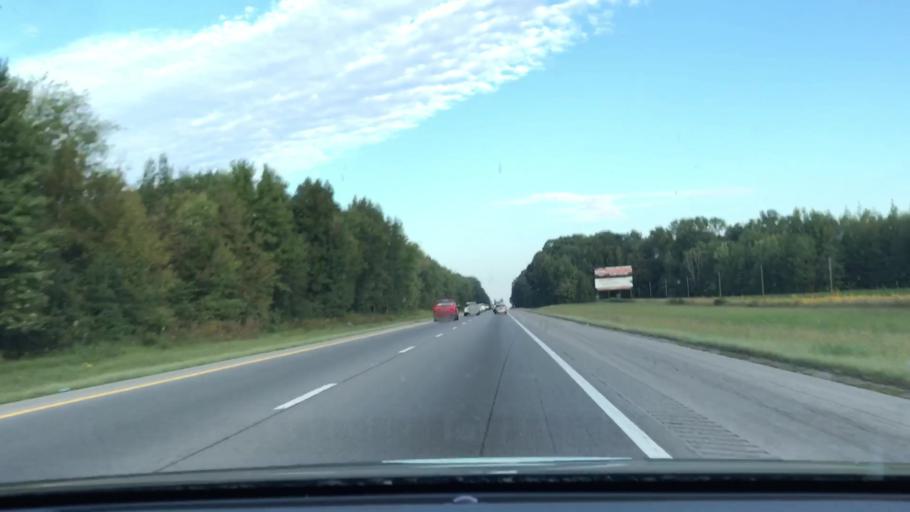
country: US
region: Tennessee
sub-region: Cheatham County
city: Pleasant View
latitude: 36.4403
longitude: -87.0840
